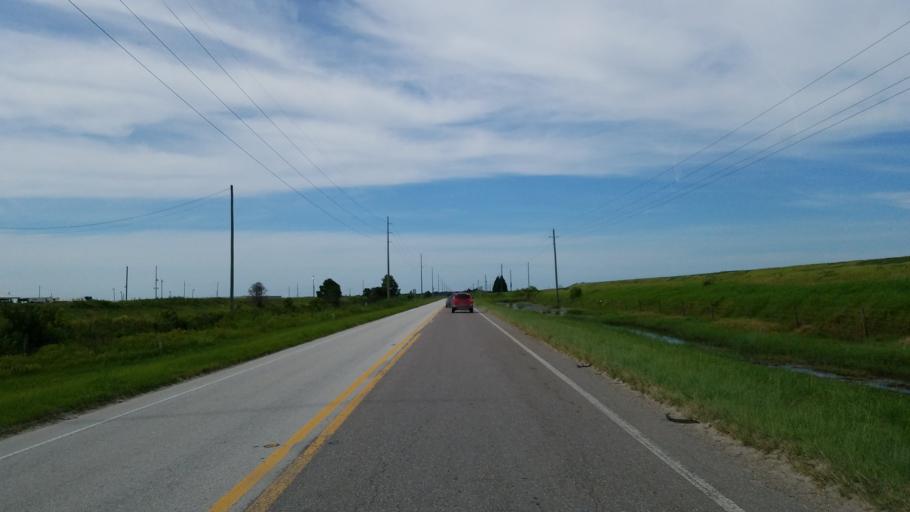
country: US
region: Florida
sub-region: Hillsborough County
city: Balm
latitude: 27.6542
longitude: -82.1464
